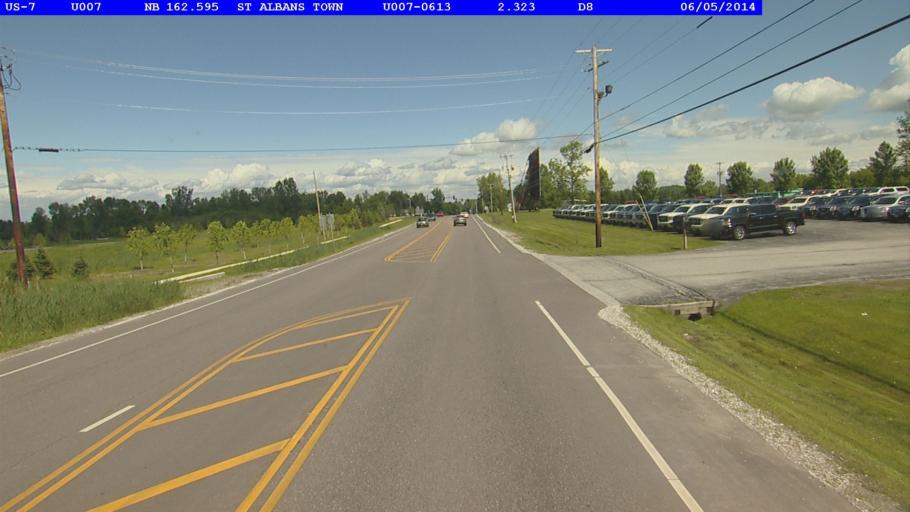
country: US
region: Vermont
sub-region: Franklin County
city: Saint Albans
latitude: 44.8415
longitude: -73.0839
